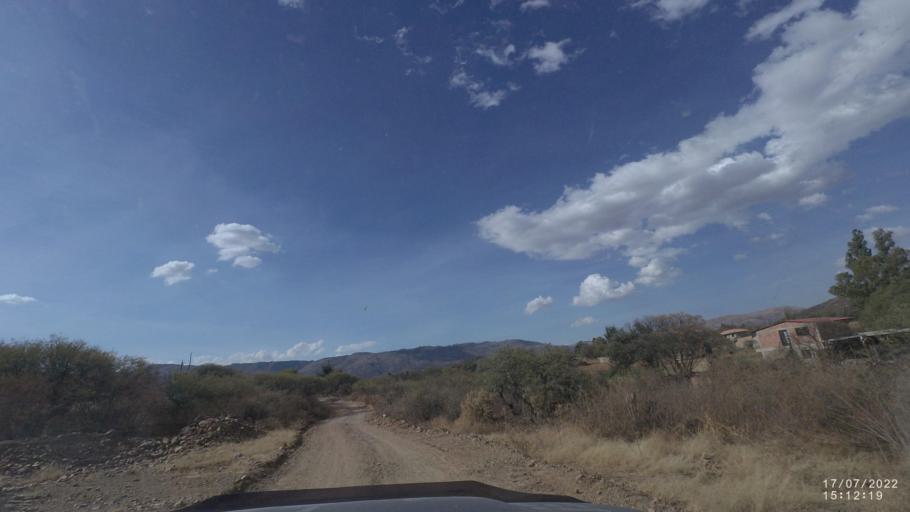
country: BO
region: Cochabamba
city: Capinota
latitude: -17.5705
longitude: -66.2637
